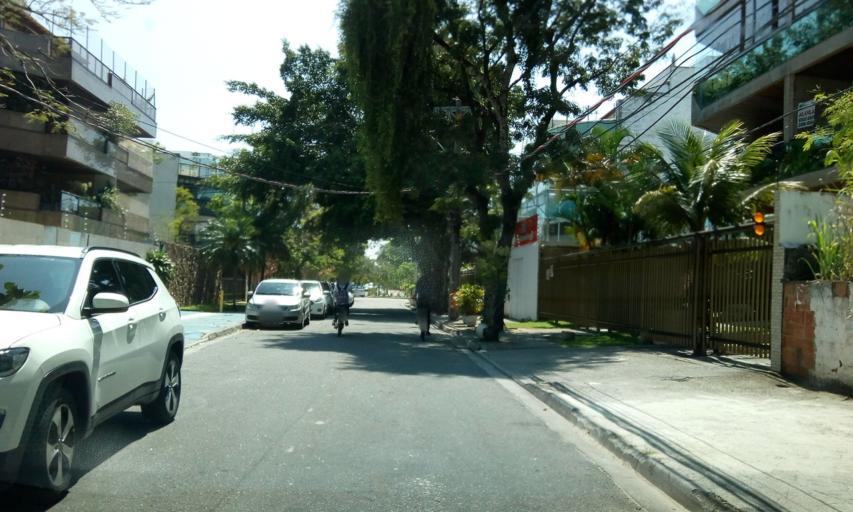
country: BR
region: Rio de Janeiro
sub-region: Nilopolis
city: Nilopolis
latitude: -23.0193
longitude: -43.4729
